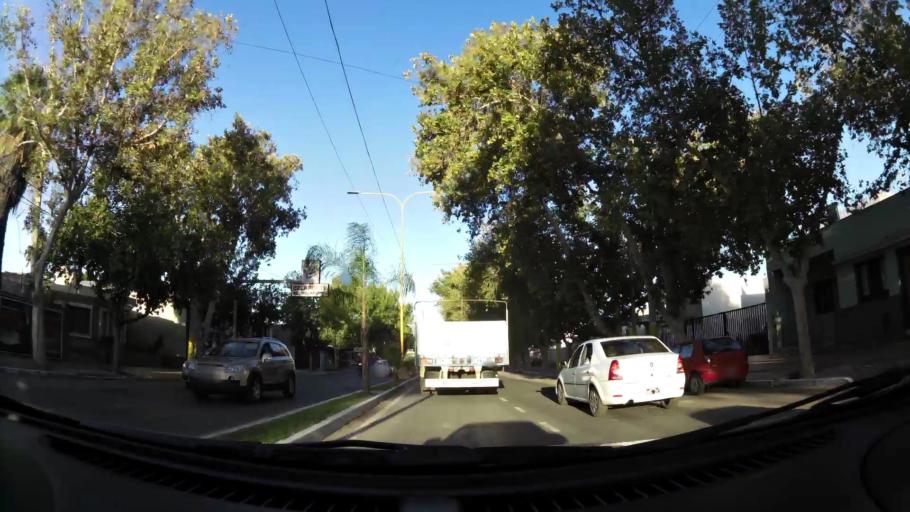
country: AR
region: San Juan
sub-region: Departamento de Santa Lucia
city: Santa Lucia
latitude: -31.5416
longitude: -68.5059
